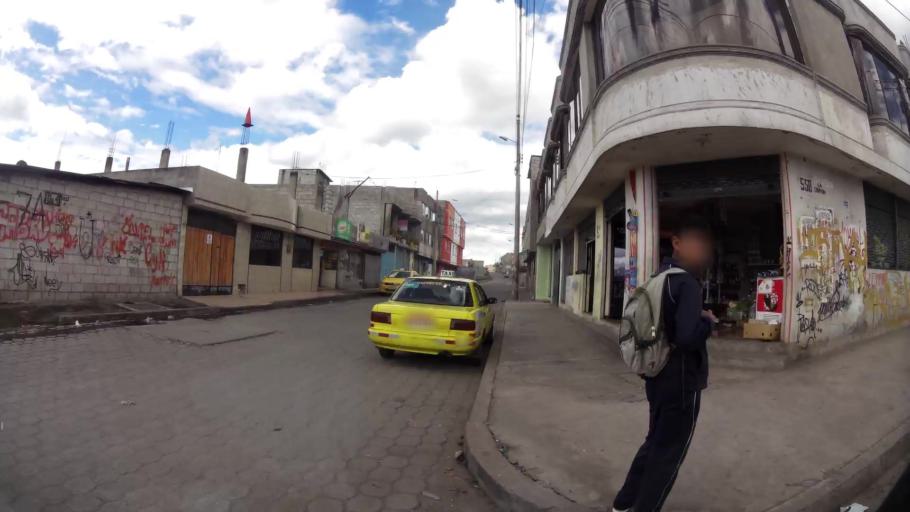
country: EC
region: Pichincha
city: Sangolqui
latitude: -0.3388
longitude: -78.5556
